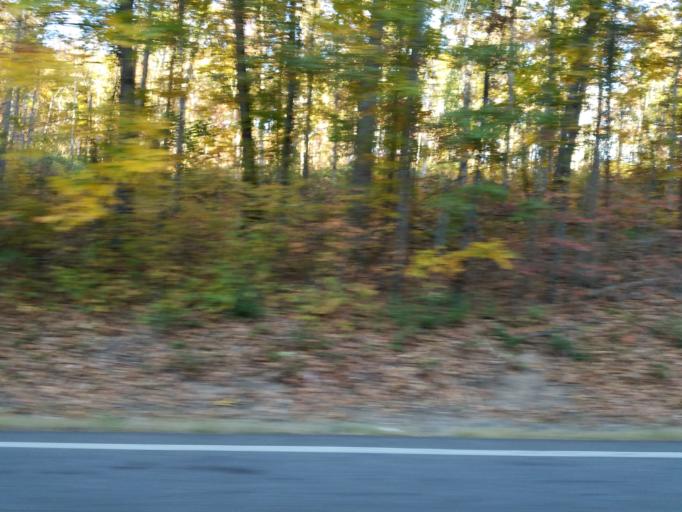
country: US
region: Georgia
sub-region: Pickens County
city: Jasper
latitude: 34.5549
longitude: -84.2940
